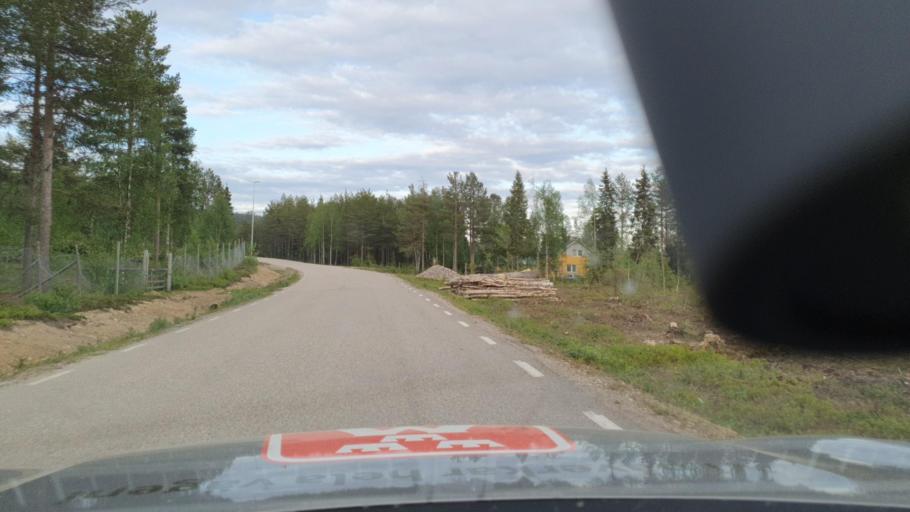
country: SE
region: Norrbotten
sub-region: Gallivare Kommun
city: Gaellivare
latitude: 66.7558
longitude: 21.0457
